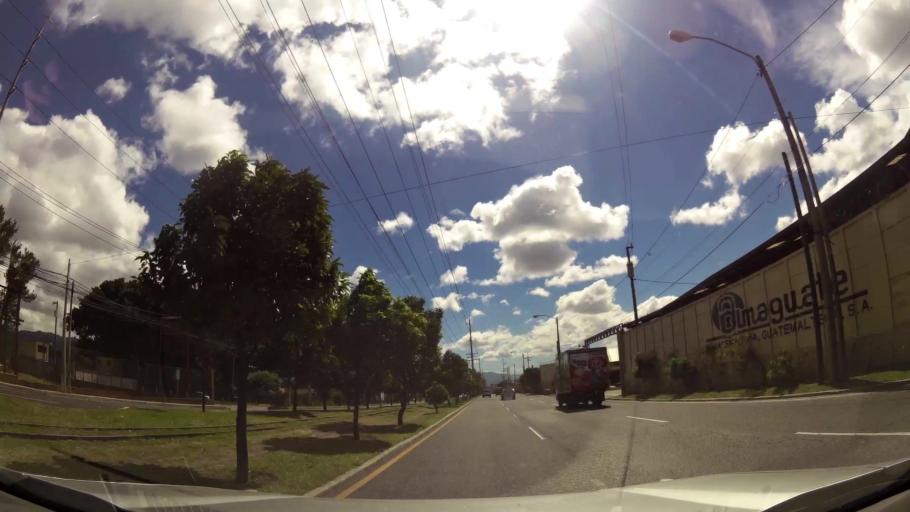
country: GT
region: Guatemala
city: Santa Catarina Pinula
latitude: 14.5818
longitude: -90.5430
